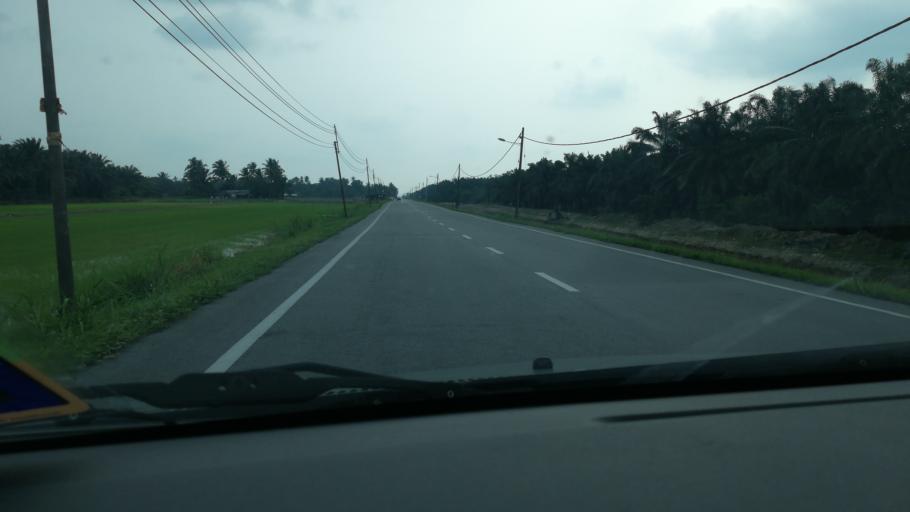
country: MY
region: Perak
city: Teluk Intan
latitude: 4.1190
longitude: 101.0771
